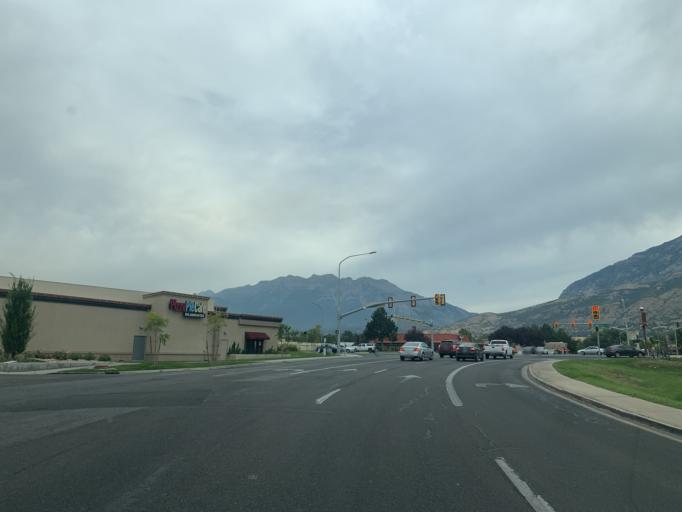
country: US
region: Utah
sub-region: Utah County
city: Provo
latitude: 40.2623
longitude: -111.6680
